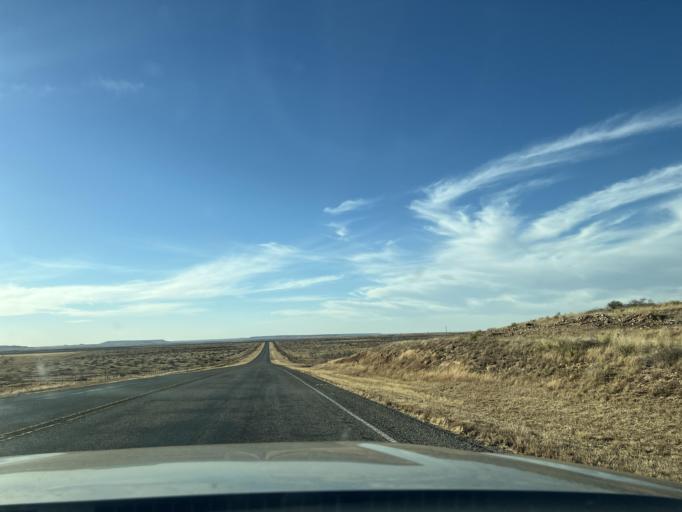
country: US
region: Texas
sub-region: Borden County
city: Gail
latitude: 32.7610
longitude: -101.2663
